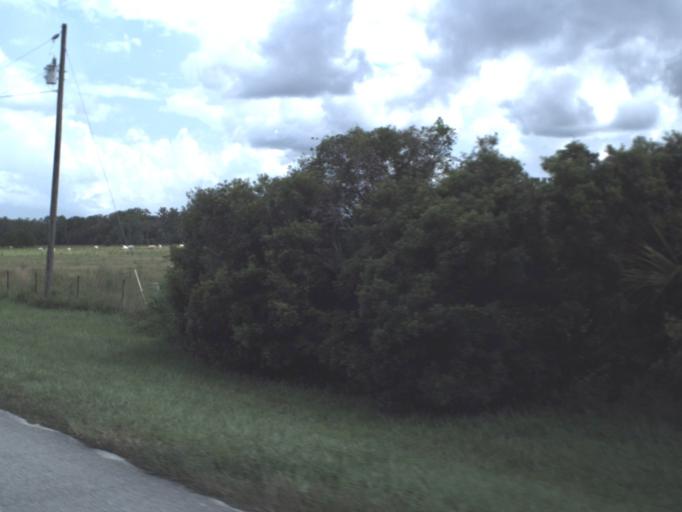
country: US
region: Florida
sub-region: DeSoto County
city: Nocatee
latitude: 27.2052
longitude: -82.0022
